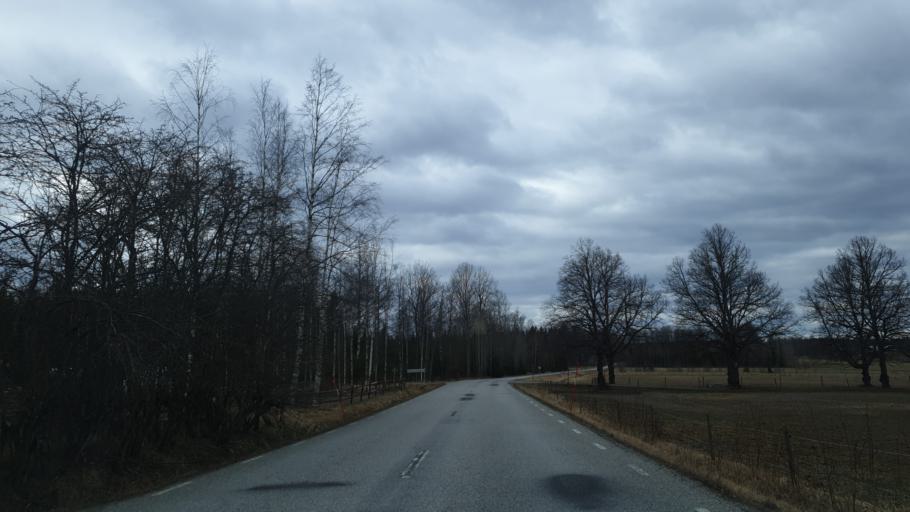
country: SE
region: OErebro
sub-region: Nora Kommun
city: As
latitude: 59.5818
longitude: 14.9699
